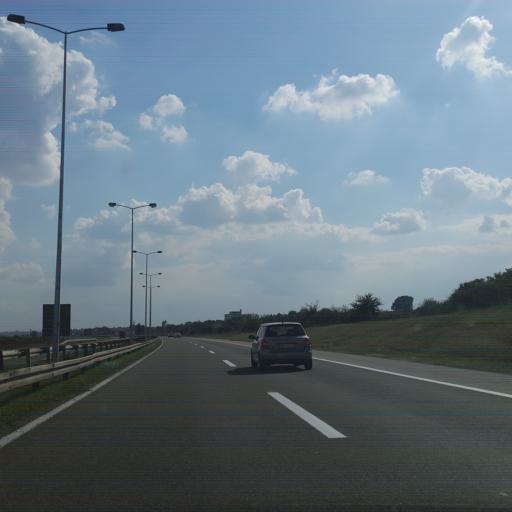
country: RS
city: Lugavcina
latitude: 44.5716
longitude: 20.9803
